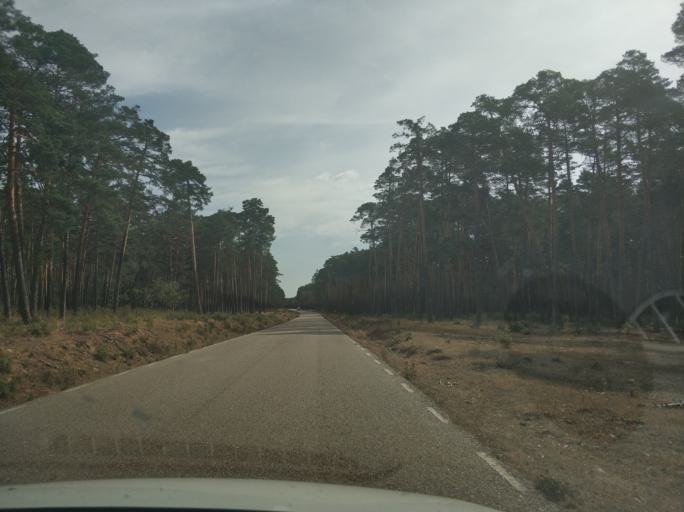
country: ES
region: Castille and Leon
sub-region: Provincia de Soria
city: Navaleno
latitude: 41.8537
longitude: -2.9586
